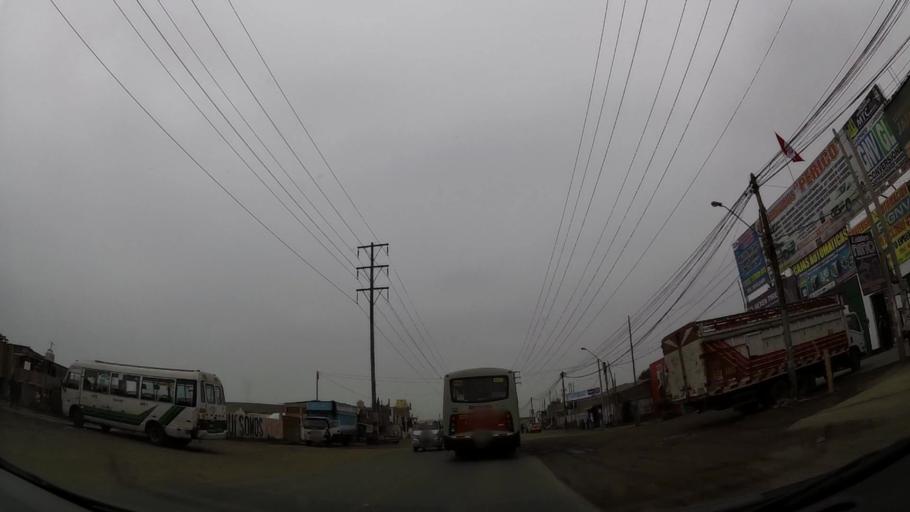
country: PE
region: Lima
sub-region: Lima
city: Punta Hermosa
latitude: -12.2705
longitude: -76.8755
